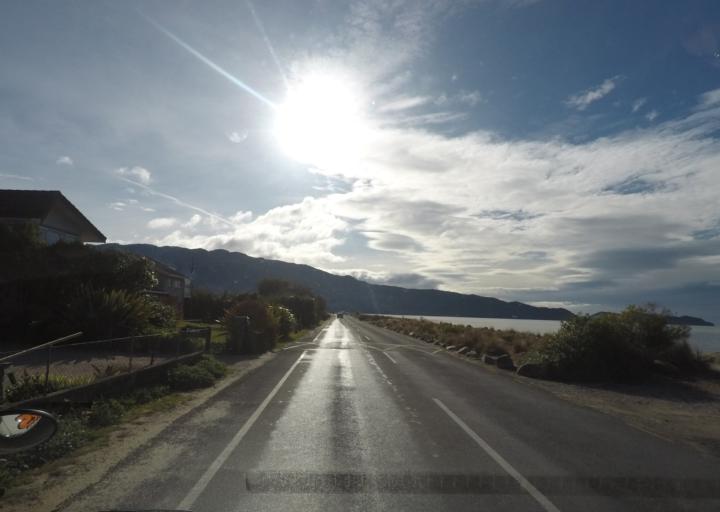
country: NZ
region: Tasman
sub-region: Tasman District
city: Motueka
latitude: -41.0073
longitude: 173.0091
